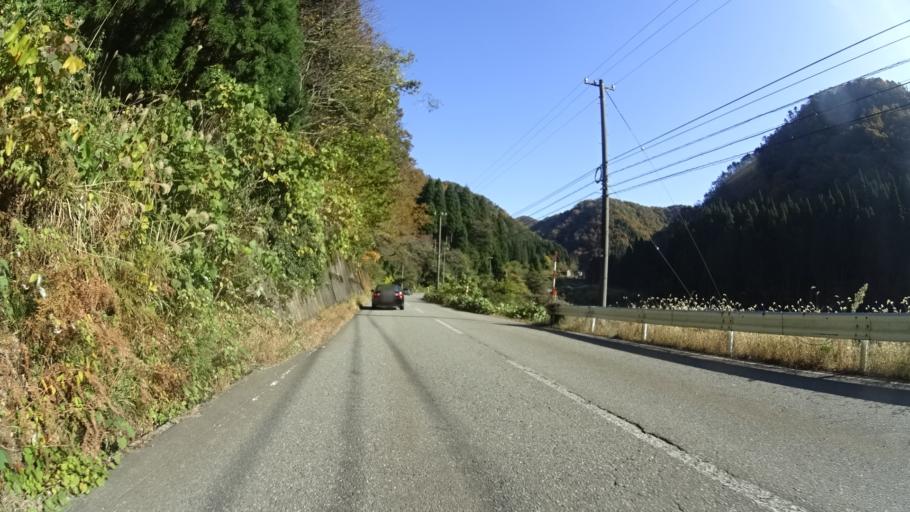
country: JP
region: Ishikawa
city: Tsurugi-asahimachi
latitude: 36.3725
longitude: 136.5621
